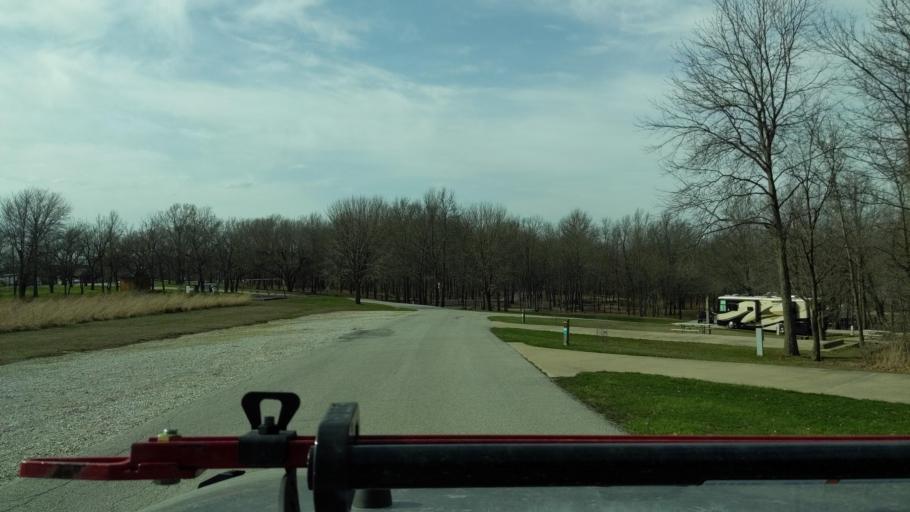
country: US
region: Missouri
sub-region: Macon County
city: Macon
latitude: 39.7699
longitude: -92.5212
